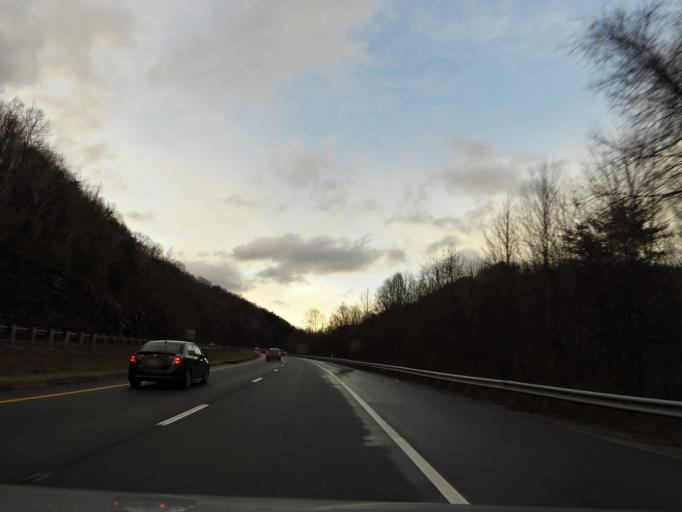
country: US
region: Tennessee
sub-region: Campbell County
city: Caryville
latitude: 36.3348
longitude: -84.2276
